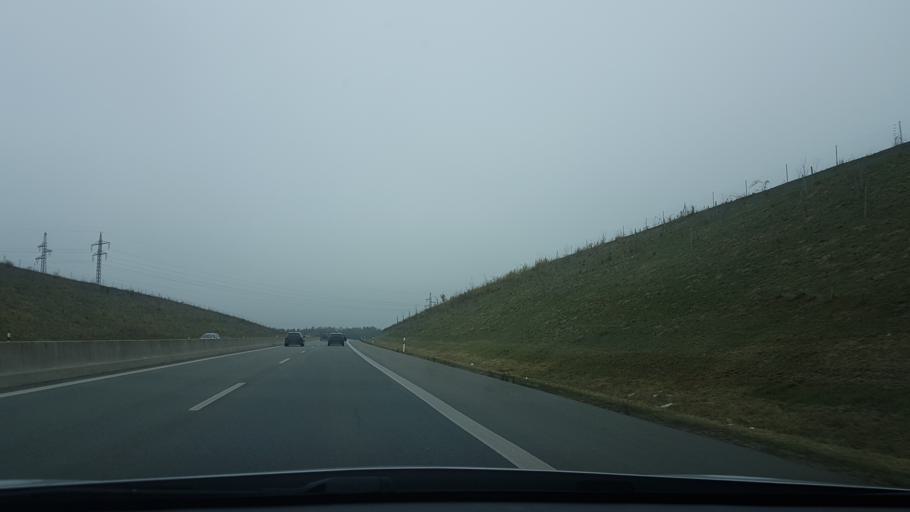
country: DE
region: Bavaria
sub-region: Lower Bavaria
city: Ergoldsbach
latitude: 48.6882
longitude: 12.1836
